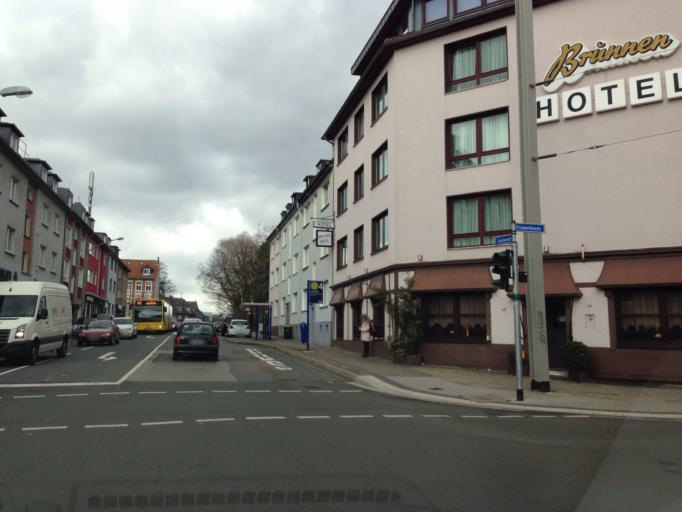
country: DE
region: North Rhine-Westphalia
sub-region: Regierungsbezirk Dusseldorf
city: Essen
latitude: 51.4396
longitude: 7.0130
